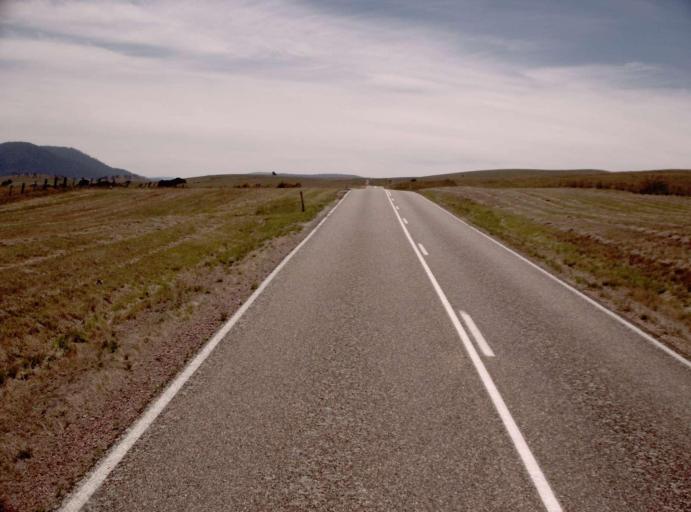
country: AU
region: Victoria
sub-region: Alpine
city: Mount Beauty
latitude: -36.9927
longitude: 147.6875
